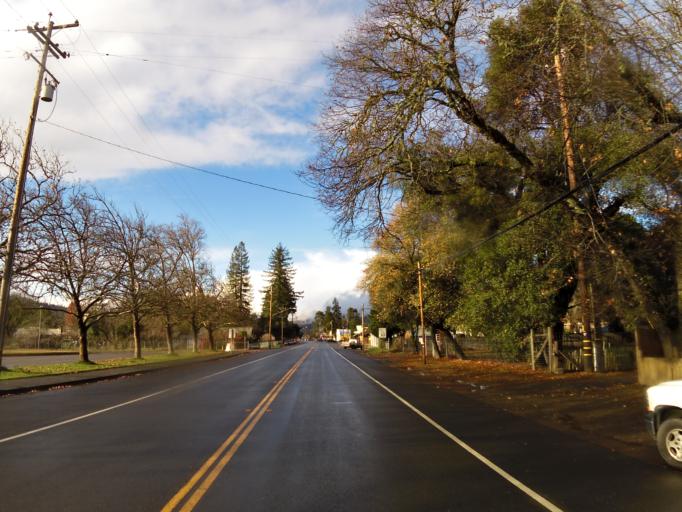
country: US
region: California
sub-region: Mendocino County
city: Boonville
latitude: 39.0053
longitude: -123.3637
